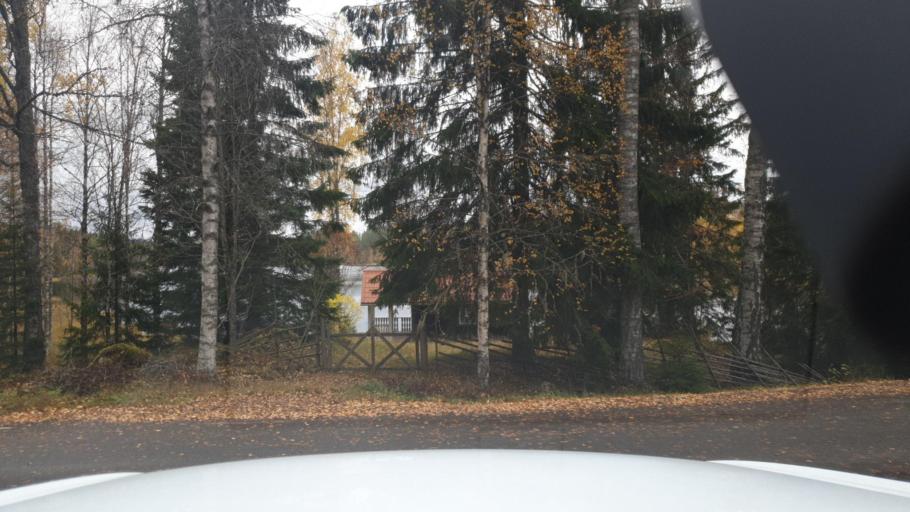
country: SE
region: Vaermland
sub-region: Eda Kommun
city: Charlottenberg
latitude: 60.0147
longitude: 12.6411
